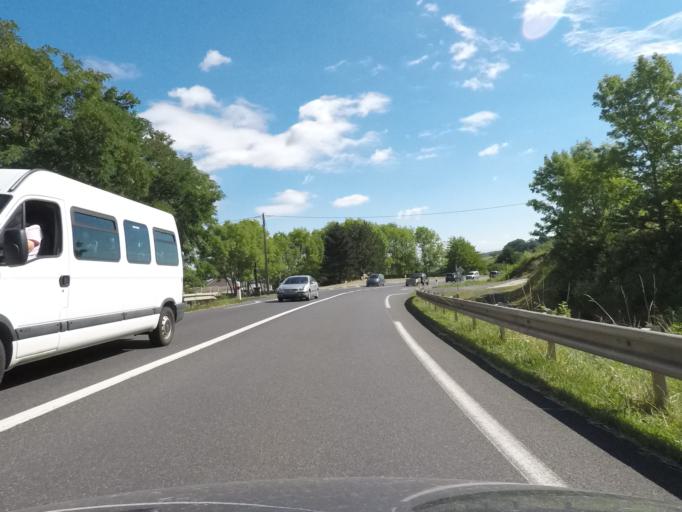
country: FR
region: Auvergne
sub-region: Departement du Puy-de-Dome
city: Ceyrat
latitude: 45.7100
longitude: 3.0708
